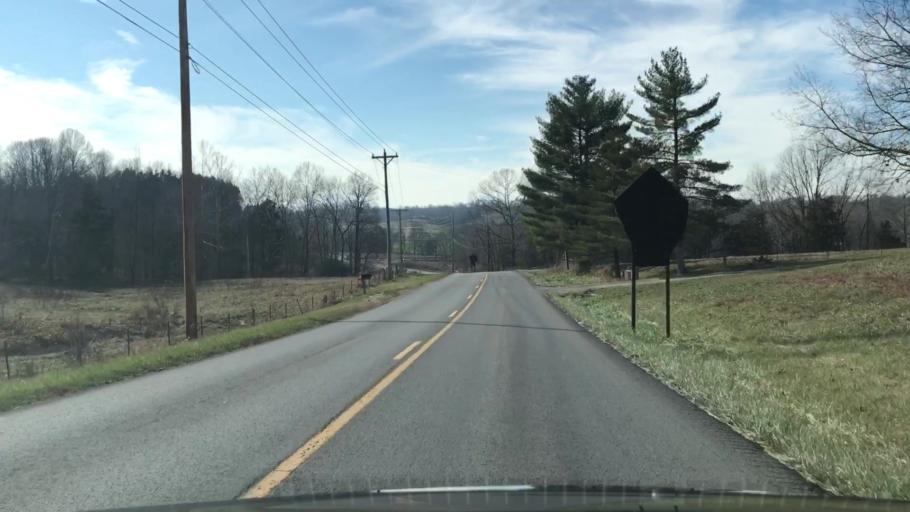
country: US
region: Kentucky
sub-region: Metcalfe County
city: Edmonton
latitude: 36.9342
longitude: -85.6351
